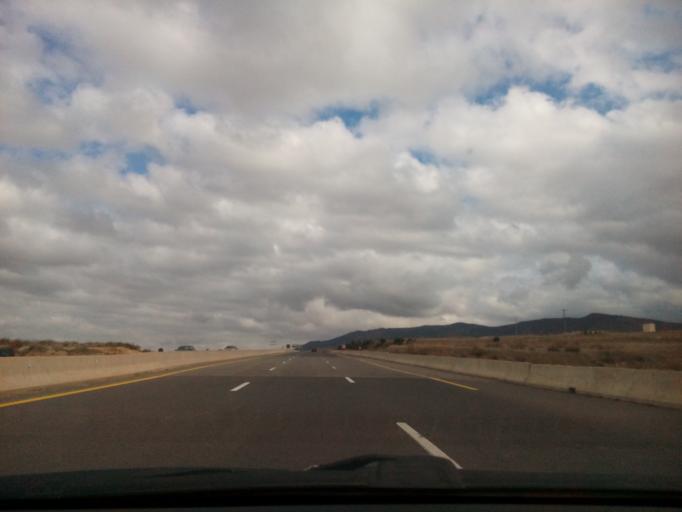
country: DZ
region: Tlemcen
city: Bensekrane
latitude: 34.9892
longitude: -1.2132
